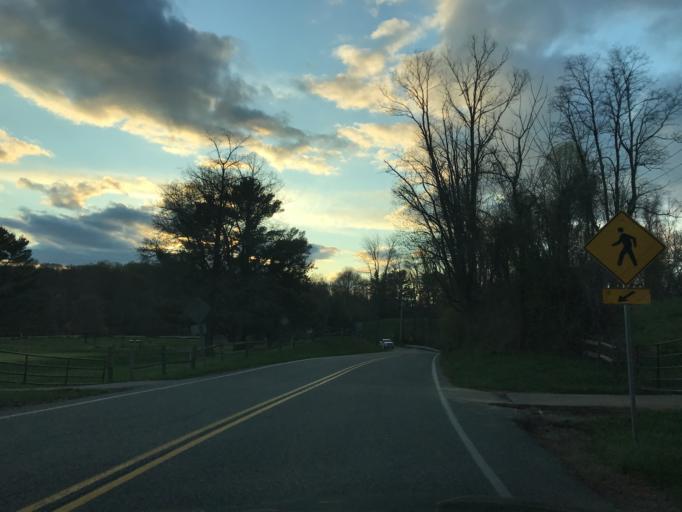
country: US
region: Maryland
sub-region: Harford County
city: Bel Air South
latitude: 39.5226
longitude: -76.3118
